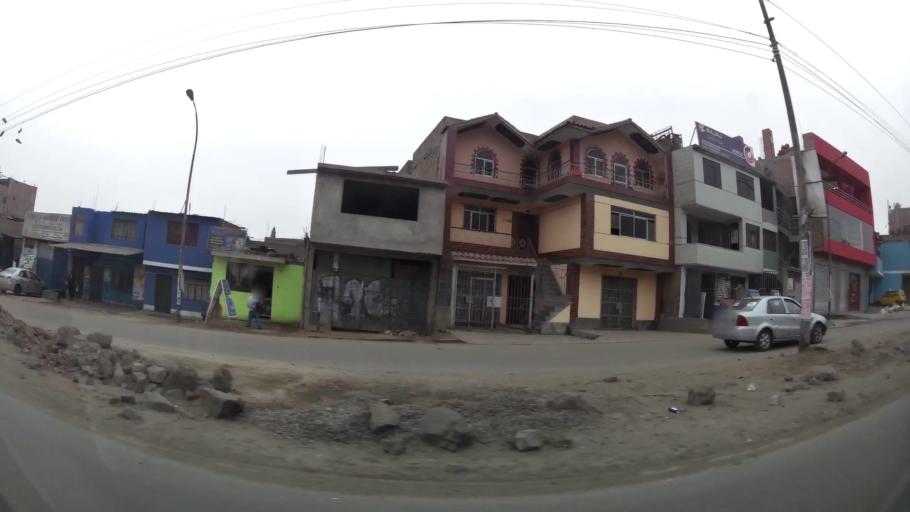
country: PE
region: Lima
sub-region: Lima
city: Urb. Santo Domingo
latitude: -11.8801
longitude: -77.0203
